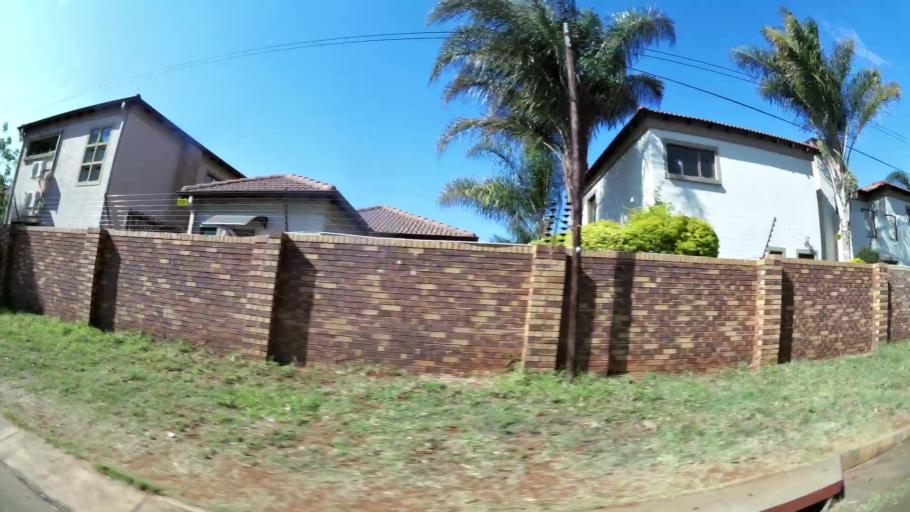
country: ZA
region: Gauteng
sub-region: City of Tshwane Metropolitan Municipality
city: Pretoria
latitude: -25.6600
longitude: 28.2503
